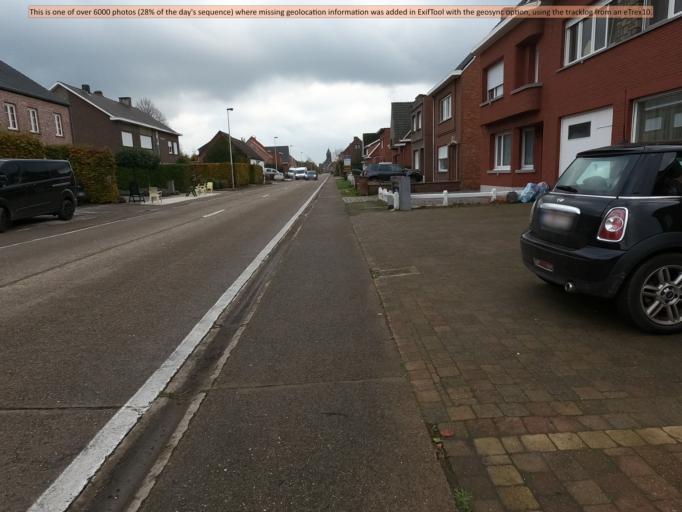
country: BE
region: Flanders
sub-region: Provincie Antwerpen
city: Nijlen
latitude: 51.1406
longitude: 4.6743
